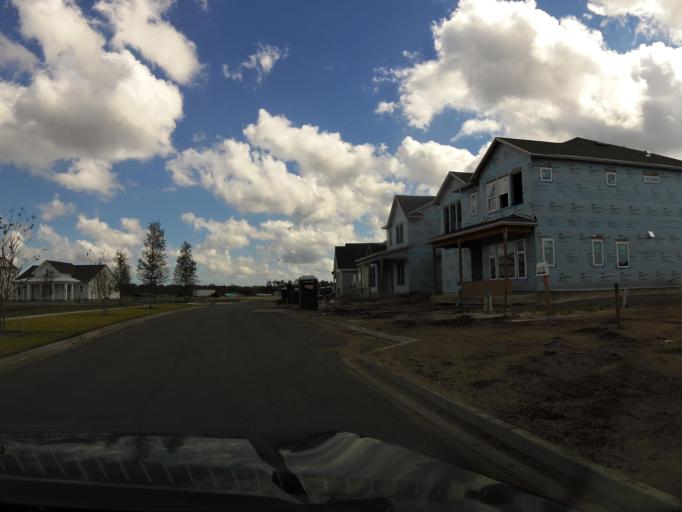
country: US
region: Florida
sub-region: Saint Johns County
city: Ponte Vedra Beach
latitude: 30.2459
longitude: -81.4963
